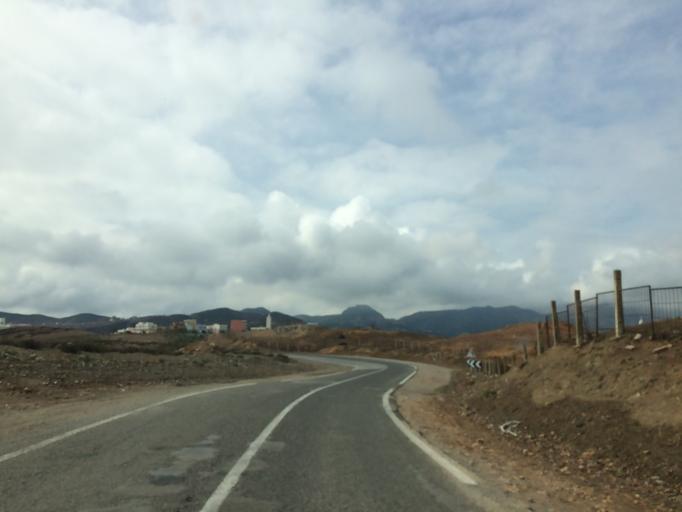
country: ES
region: Ceuta
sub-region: Ceuta
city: Ceuta
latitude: 35.8687
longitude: -5.3526
